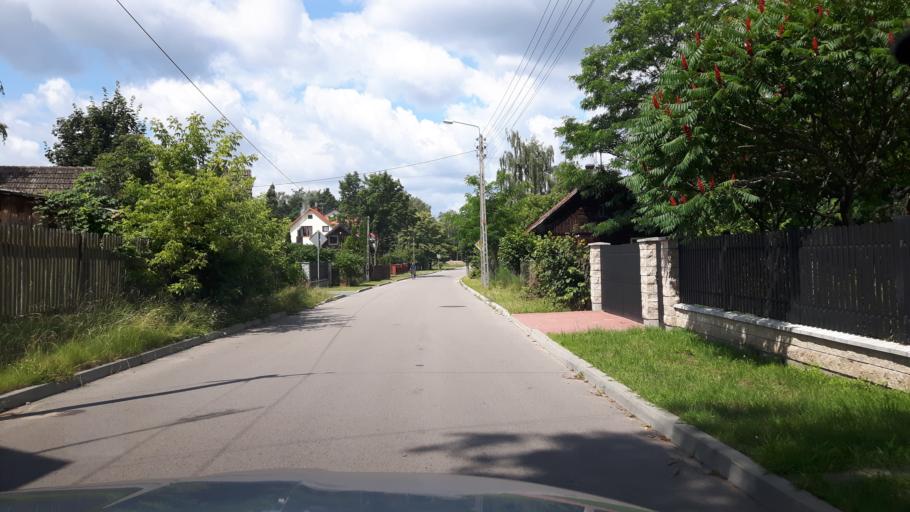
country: PL
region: Masovian Voivodeship
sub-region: Powiat ostrowski
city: Brok
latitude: 52.6994
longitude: 21.8563
